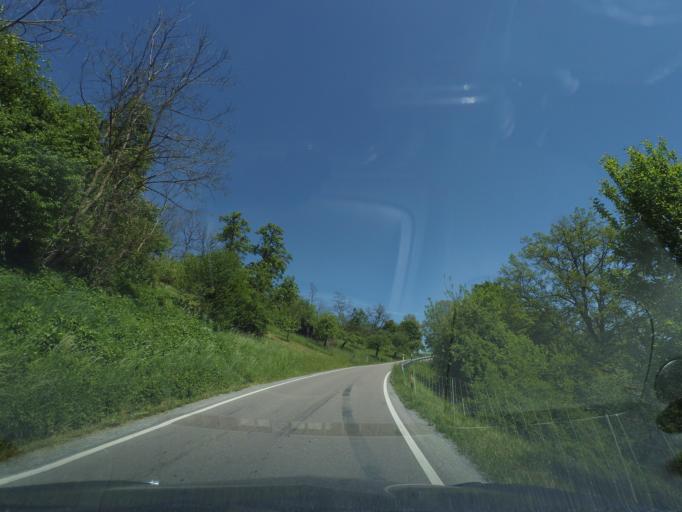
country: DE
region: Baden-Wuerttemberg
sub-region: Regierungsbezirk Stuttgart
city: Oberrot
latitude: 49.0040
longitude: 9.6896
